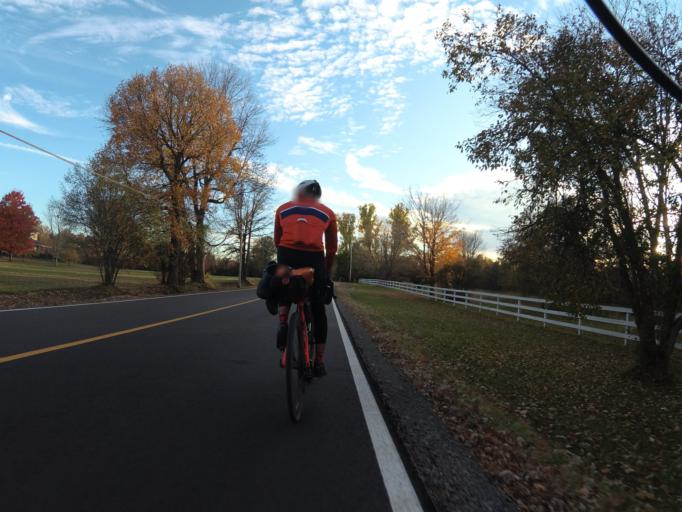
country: CA
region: Ontario
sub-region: Lanark County
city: Smiths Falls
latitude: 44.9449
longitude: -75.8205
